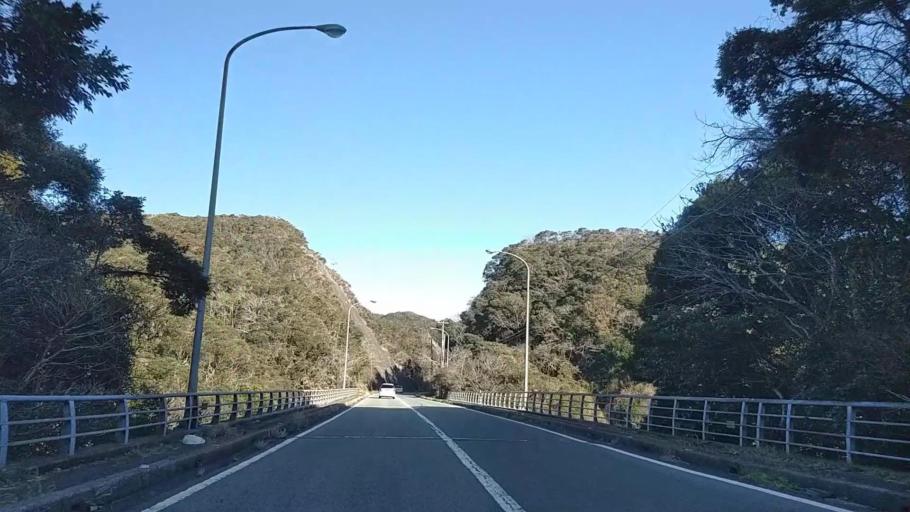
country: JP
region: Chiba
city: Katsuura
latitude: 35.1413
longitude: 140.2585
